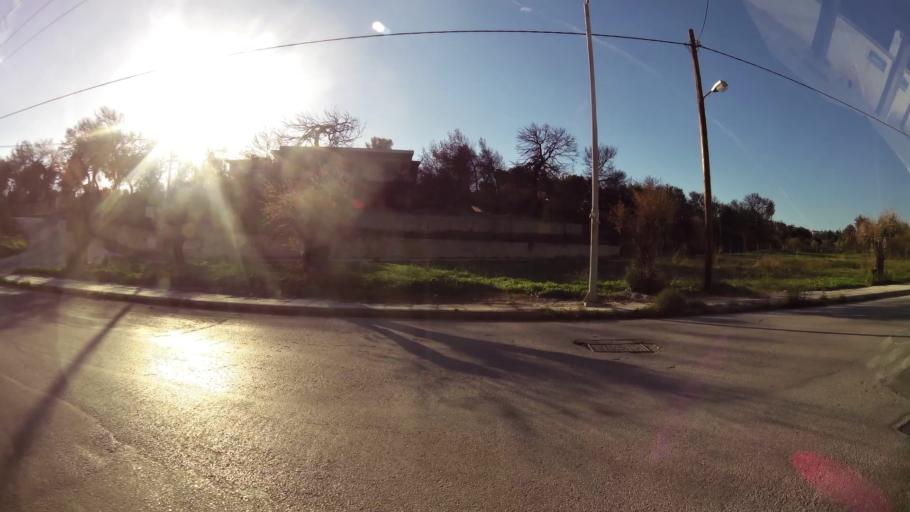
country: GR
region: Attica
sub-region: Nomarchia Anatolikis Attikis
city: Rafina
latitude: 38.0222
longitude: 23.9966
